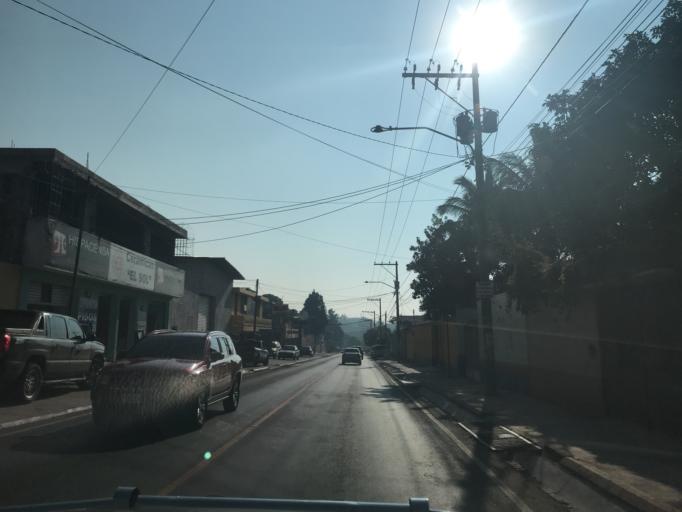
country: GT
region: Guatemala
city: Amatitlan
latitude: 14.4874
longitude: -90.6209
